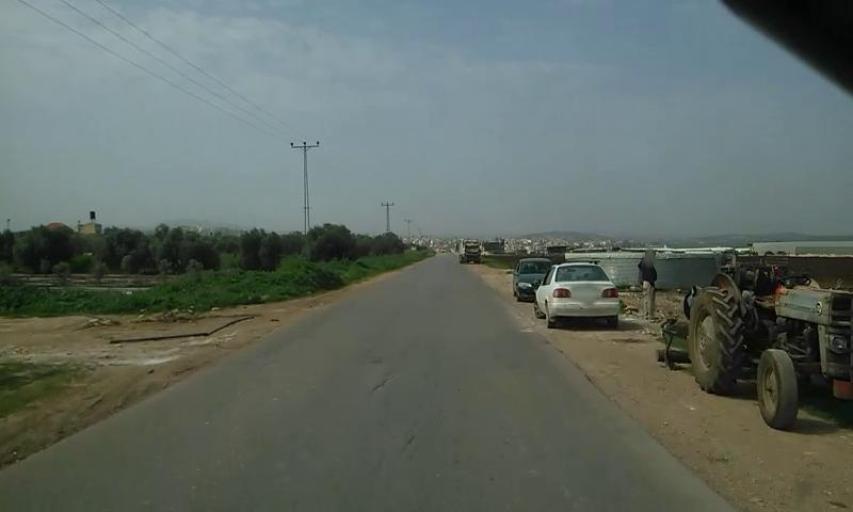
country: PS
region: West Bank
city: Kafr Dan
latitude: 32.4999
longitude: 35.2481
